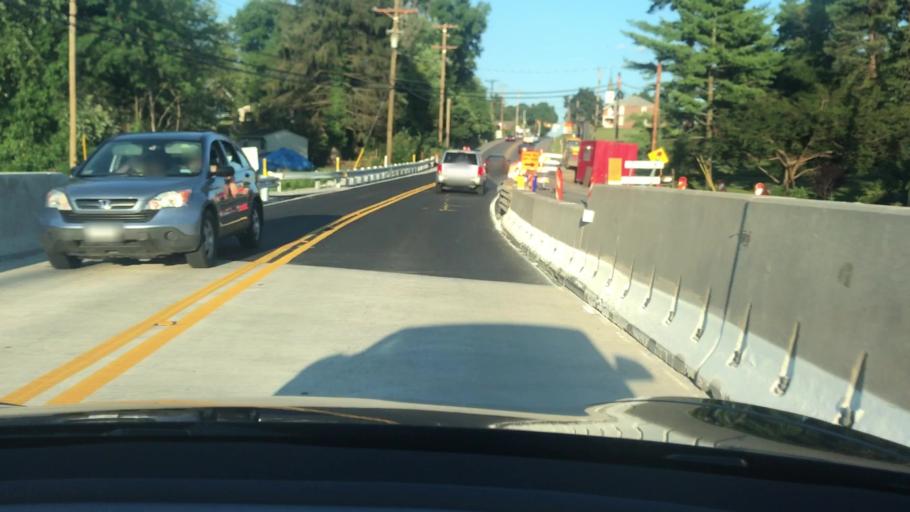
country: US
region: Pennsylvania
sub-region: York County
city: Shiloh
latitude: 39.9807
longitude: -76.8065
